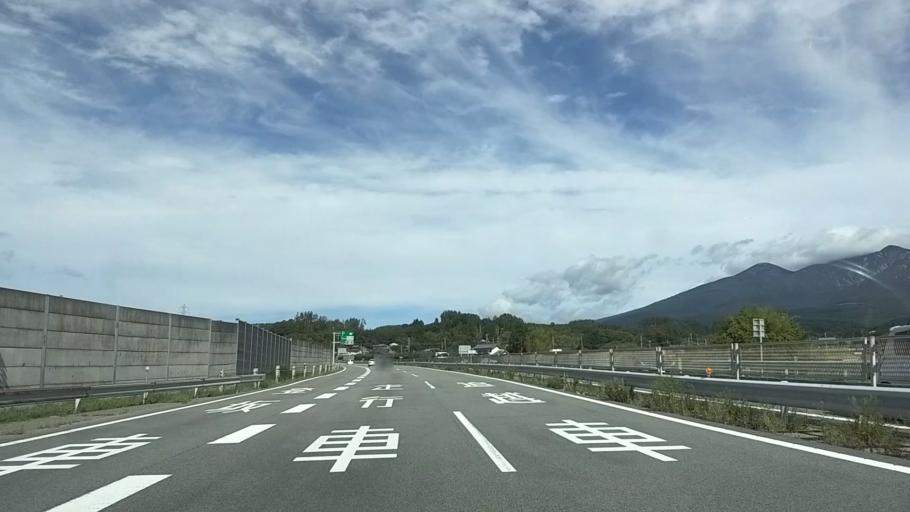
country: JP
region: Yamanashi
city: Nirasaki
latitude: 35.8407
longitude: 138.3821
